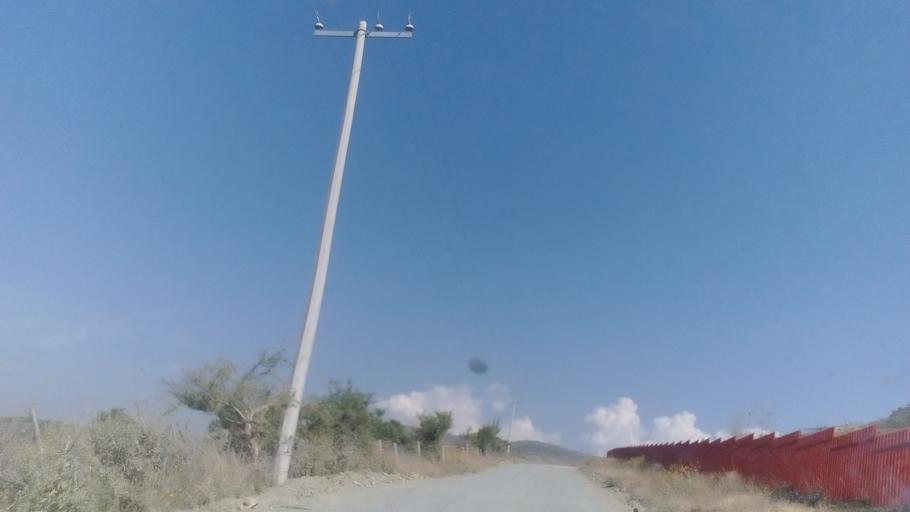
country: MX
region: Guanajuato
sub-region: Leon
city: Medina
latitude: 21.1442
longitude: -101.6029
